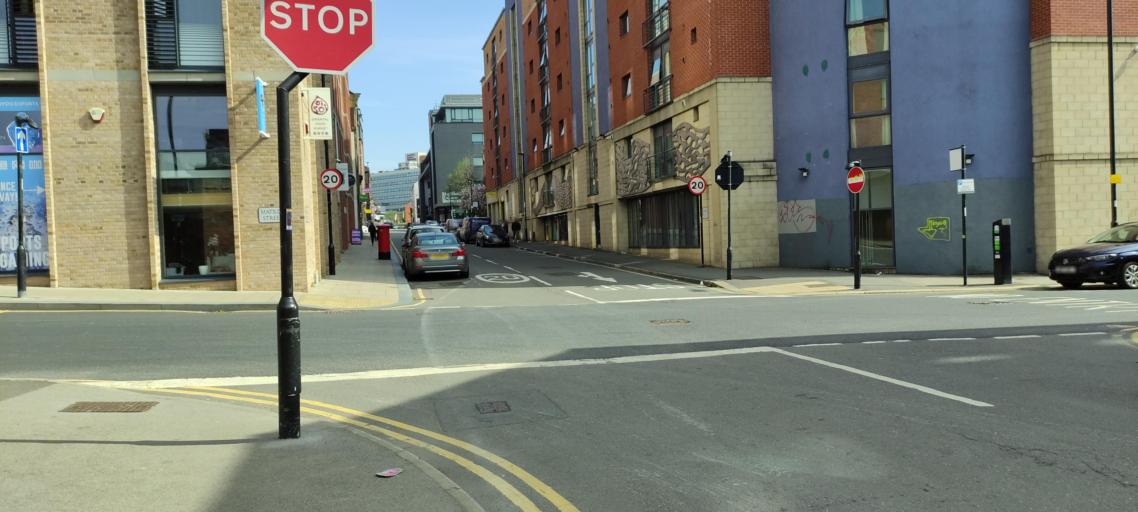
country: GB
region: England
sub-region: Sheffield
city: Sheffield
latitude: 53.3756
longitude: -1.4697
